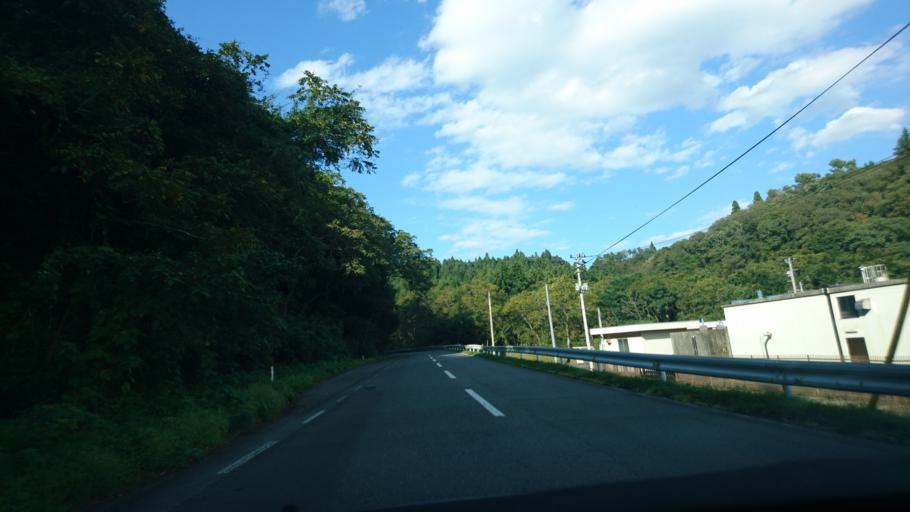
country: JP
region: Iwate
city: Ichinoseki
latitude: 38.8543
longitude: 141.3029
